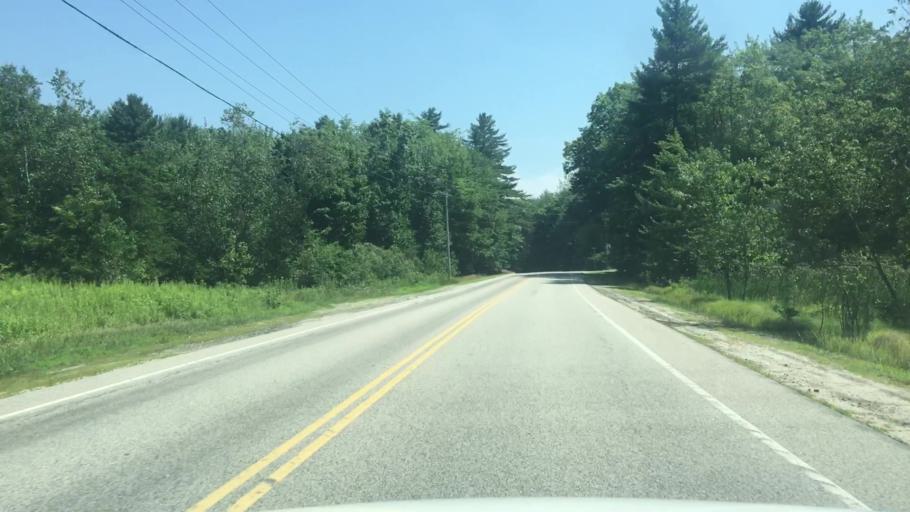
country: US
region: Maine
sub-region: Cumberland County
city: Falmouth
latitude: 43.7370
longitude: -70.2464
